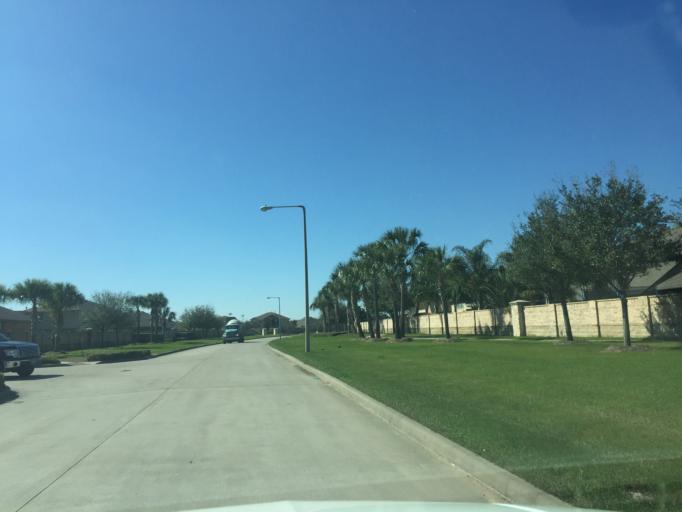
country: US
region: Texas
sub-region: Galveston County
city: Bacliff
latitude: 29.5114
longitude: -95.0165
